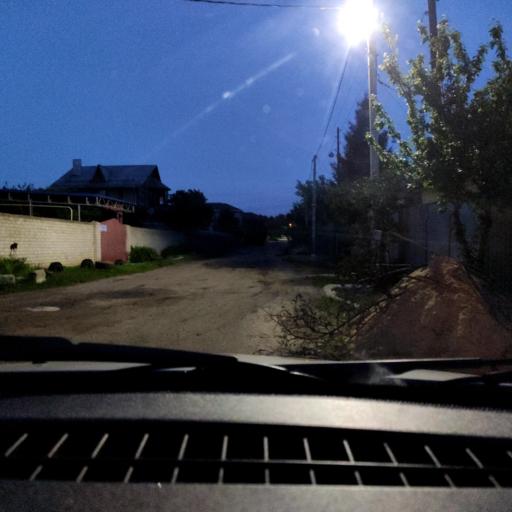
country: RU
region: Voronezj
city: Pridonskoy
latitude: 51.6393
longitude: 39.0810
